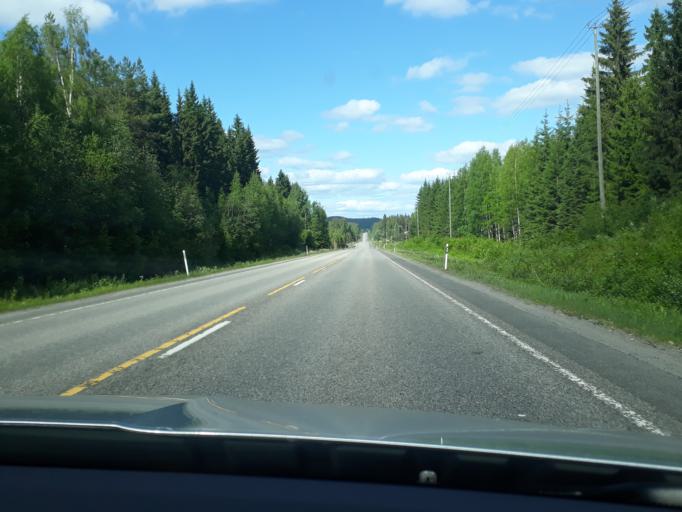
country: FI
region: Central Finland
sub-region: AEaenekoski
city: AEaenekoski
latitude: 62.6511
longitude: 25.7176
